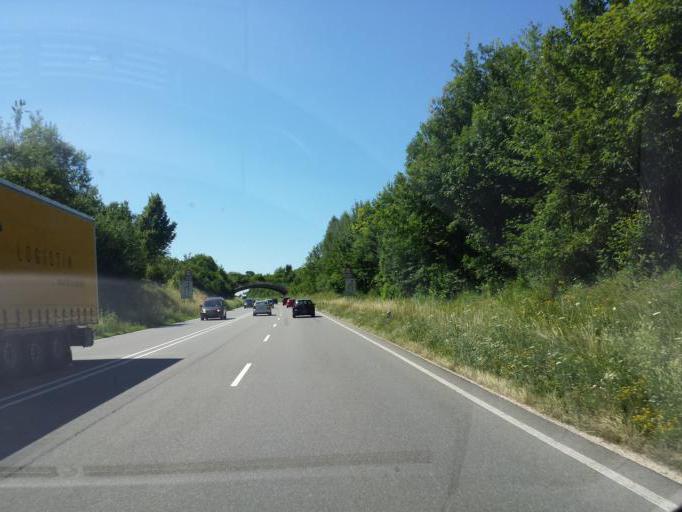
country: DE
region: Baden-Wuerttemberg
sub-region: Tuebingen Region
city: Sipplingen
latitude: 47.8139
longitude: 9.1118
